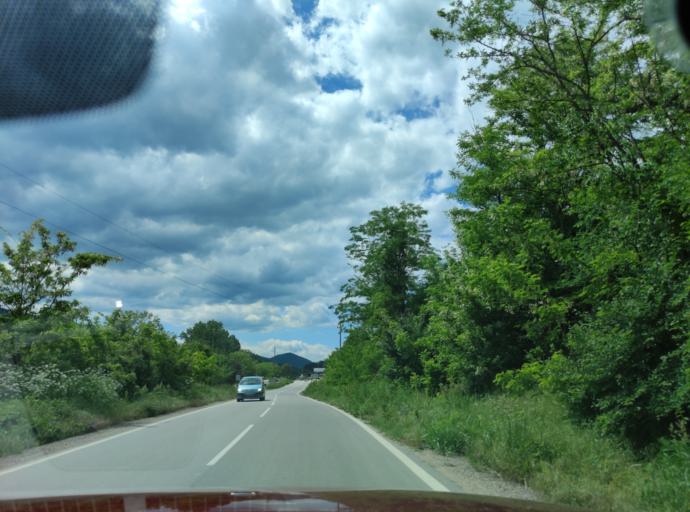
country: BG
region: Montana
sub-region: Obshtina Chiprovtsi
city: Chiprovtsi
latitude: 43.4381
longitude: 22.9432
